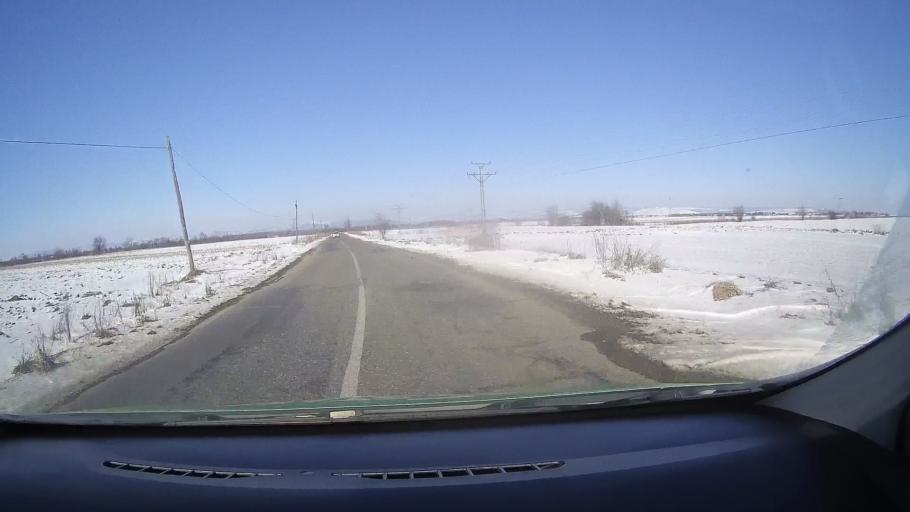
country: RO
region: Brasov
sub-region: Comuna Harseni
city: Harseni
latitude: 45.7680
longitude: 25.0037
